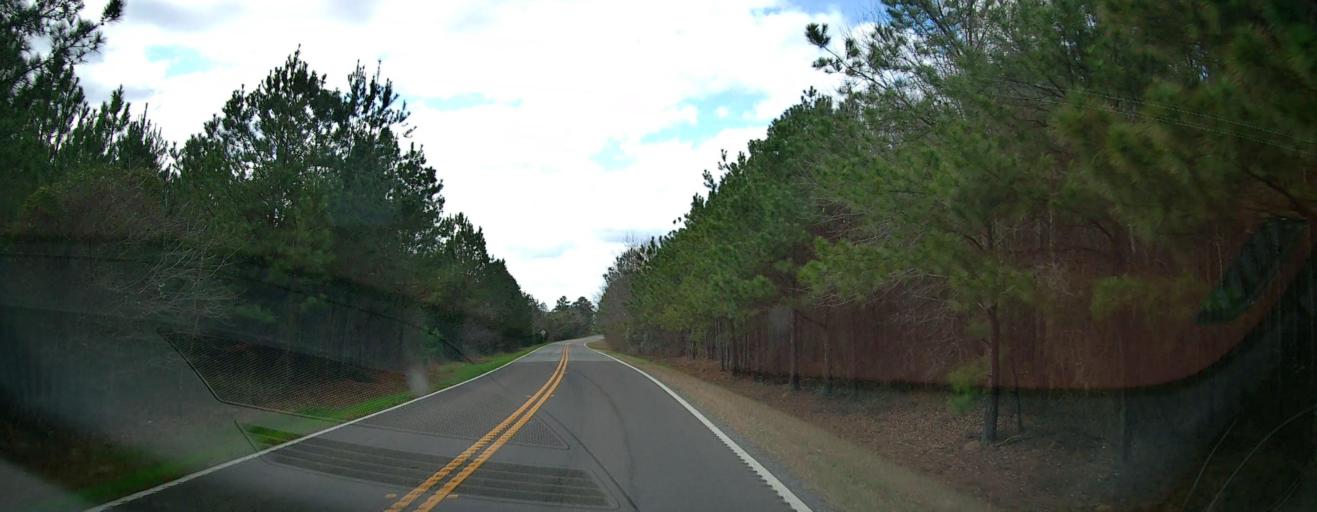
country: US
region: Georgia
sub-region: Marion County
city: Buena Vista
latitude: 32.4339
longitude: -84.4293
